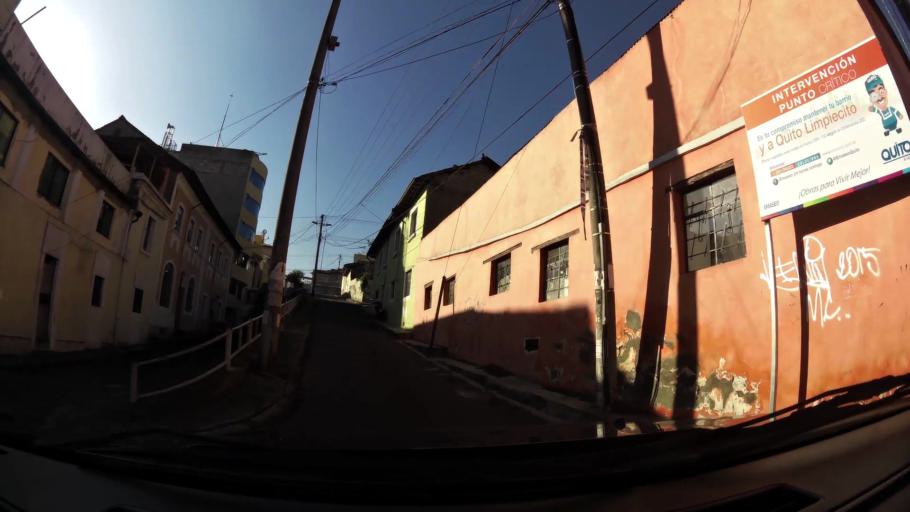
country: EC
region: Pichincha
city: Quito
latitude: -0.2414
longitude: -78.5154
